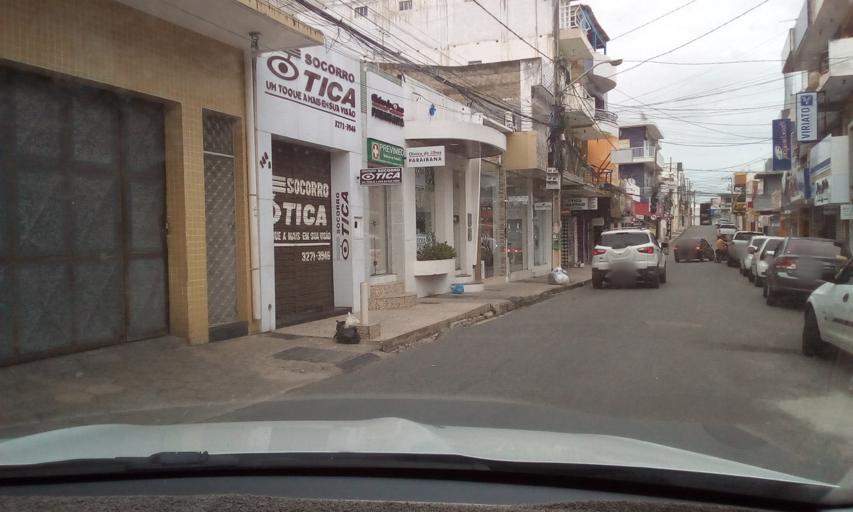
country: BR
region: Paraiba
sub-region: Guarabira
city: Guarabira
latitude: -6.8517
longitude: -35.4906
